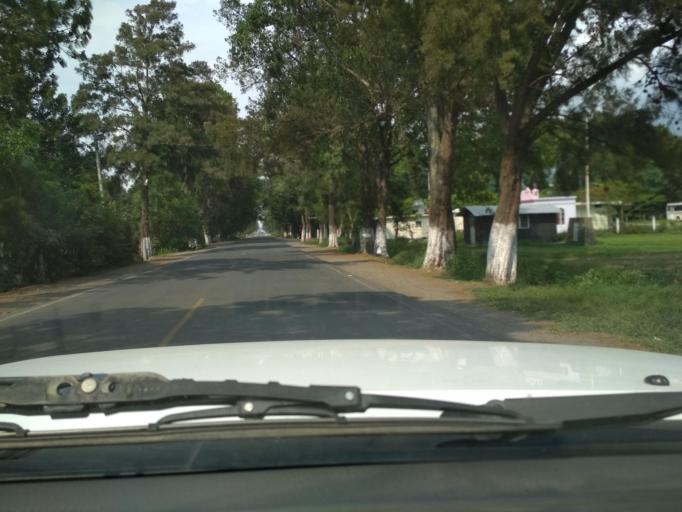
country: MX
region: Veracruz
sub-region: Acultzingo
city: Sierra de Agua
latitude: 18.7556
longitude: -97.2337
